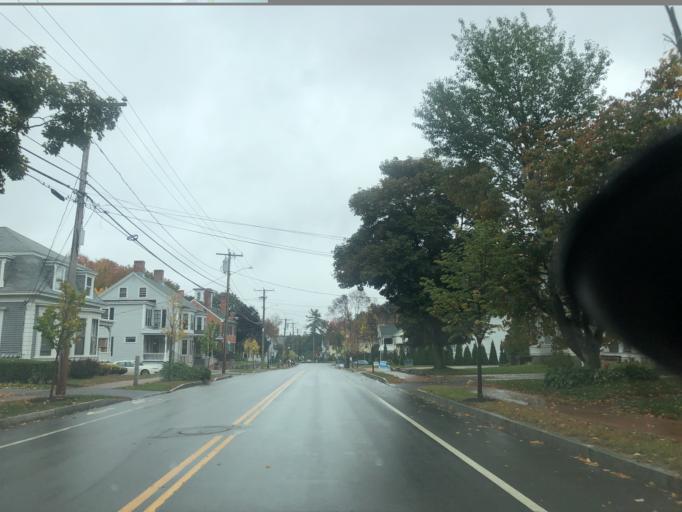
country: US
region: New Hampshire
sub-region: Strafford County
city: Dover
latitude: 43.1907
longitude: -70.8791
